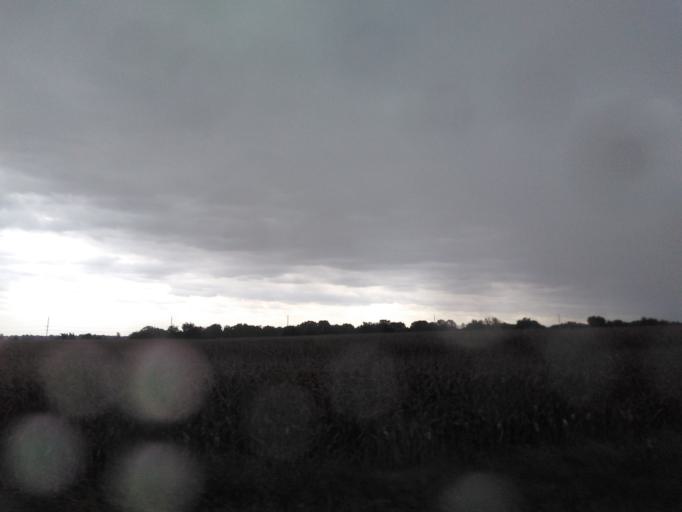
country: US
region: Illinois
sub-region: Madison County
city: Highland
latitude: 38.7509
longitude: -89.6684
